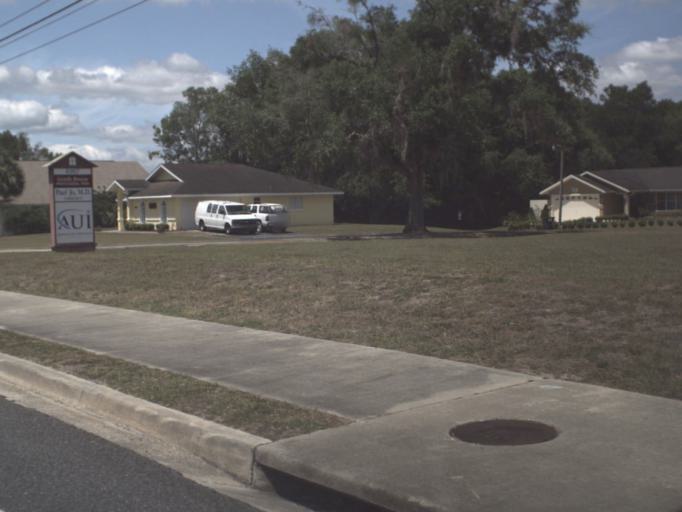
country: US
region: Florida
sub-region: Marion County
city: Ocala
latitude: 29.1028
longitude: -82.2334
